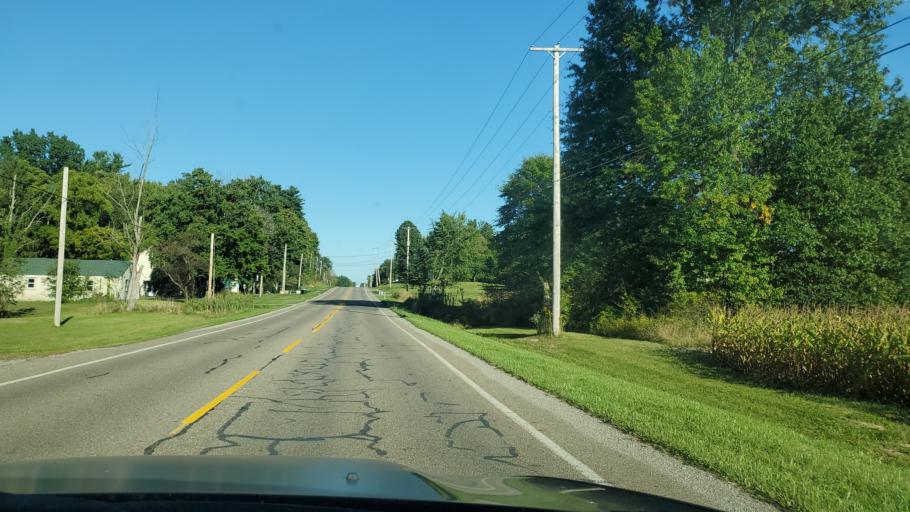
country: US
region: Ohio
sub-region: Mahoning County
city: Canfield
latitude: 40.9883
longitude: -80.7871
